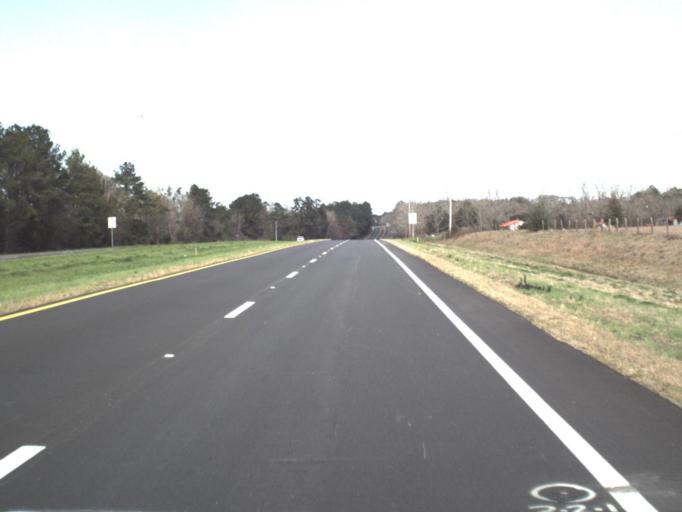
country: US
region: Florida
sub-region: Washington County
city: Chipley
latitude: 30.6836
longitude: -85.3932
